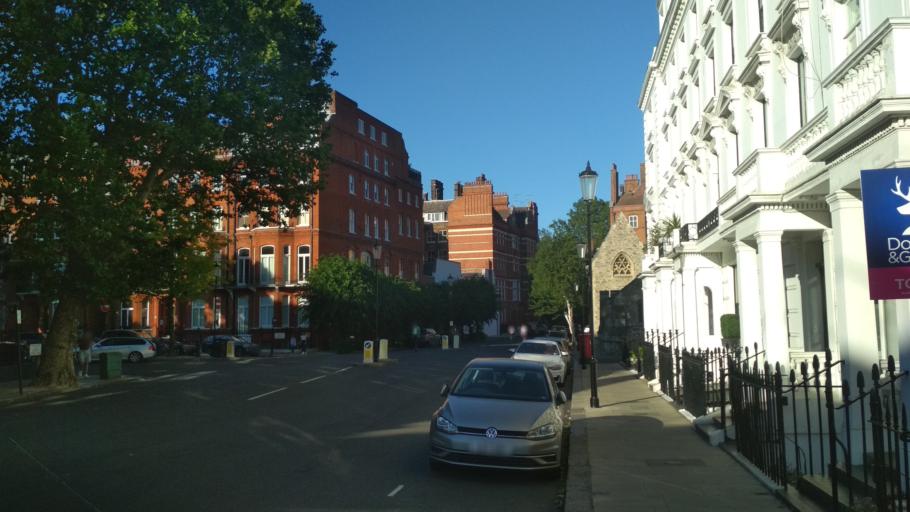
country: GB
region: England
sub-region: Greater London
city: Chelsea
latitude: 51.4945
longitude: -0.1632
